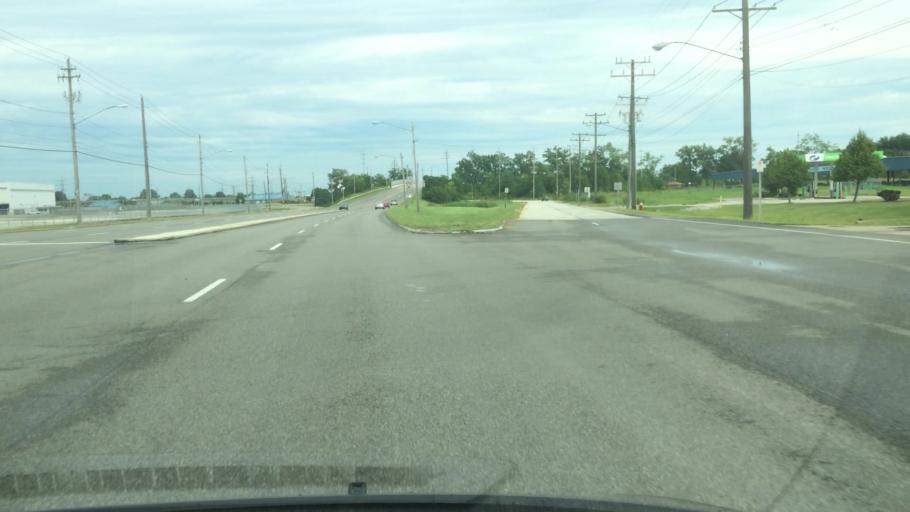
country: US
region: Ohio
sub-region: Cuyahoga County
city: Brook Park
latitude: 41.4036
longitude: -81.8301
